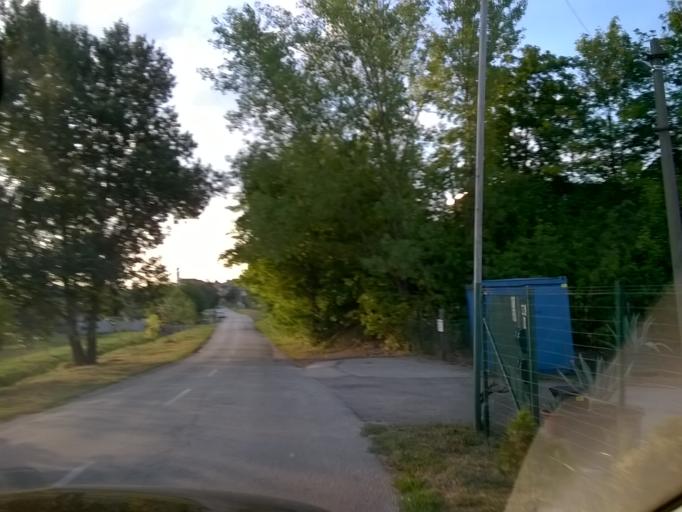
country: SK
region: Nitriansky
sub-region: Okres Nitra
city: Nitra
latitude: 48.2772
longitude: 17.9467
